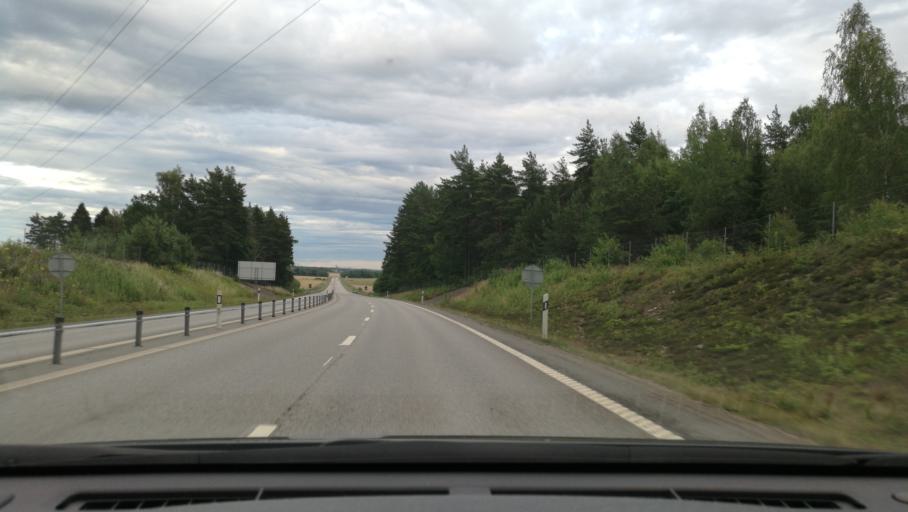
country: SE
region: OEstergoetland
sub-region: Norrkopings Kommun
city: Jursla
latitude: 58.6351
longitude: 16.1060
